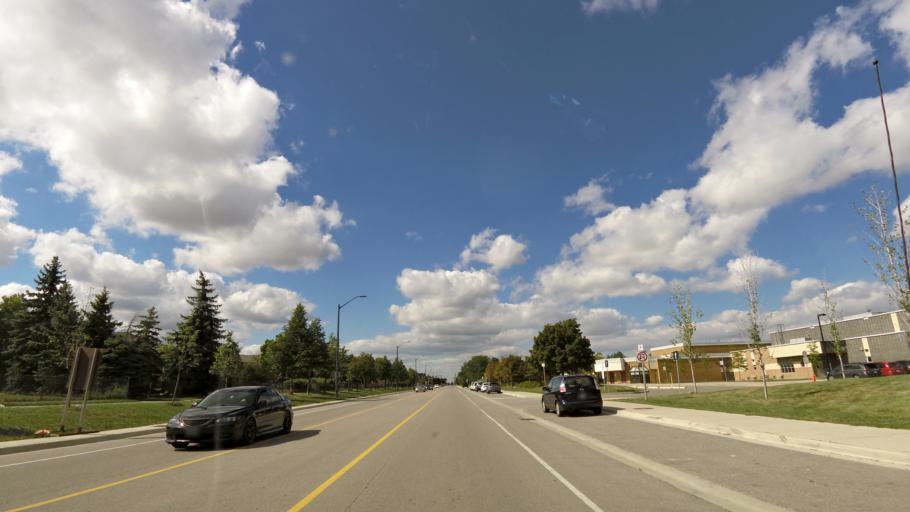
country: CA
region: Ontario
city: Brampton
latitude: 43.5800
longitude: -79.7709
